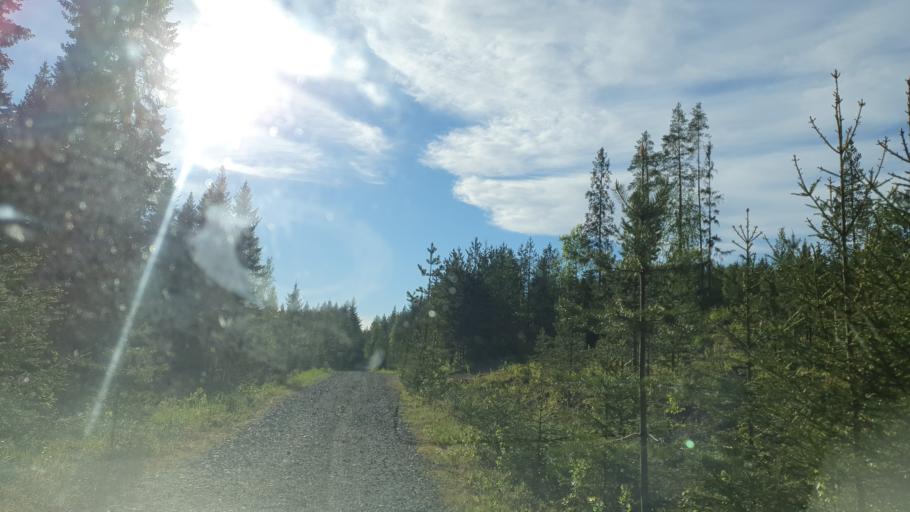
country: FI
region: Kainuu
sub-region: Kehys-Kainuu
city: Kuhmo
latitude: 64.1793
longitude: 29.4203
